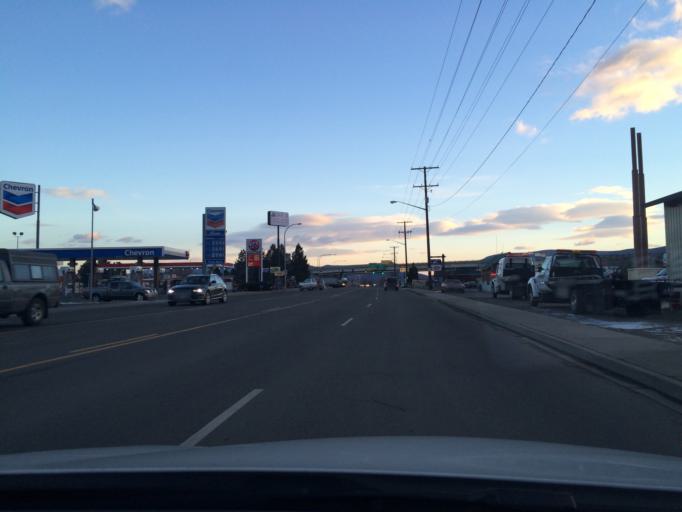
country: US
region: Washington
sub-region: Kittitas County
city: Ellensburg
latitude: 46.9763
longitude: -120.5425
